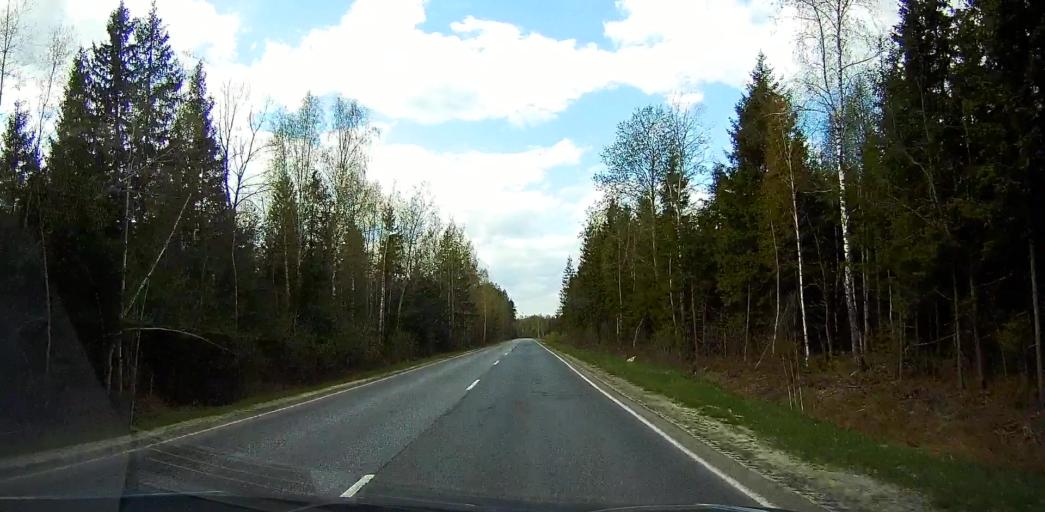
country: RU
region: Moskovskaya
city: Rakhmanovo
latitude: 55.6493
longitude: 38.6648
